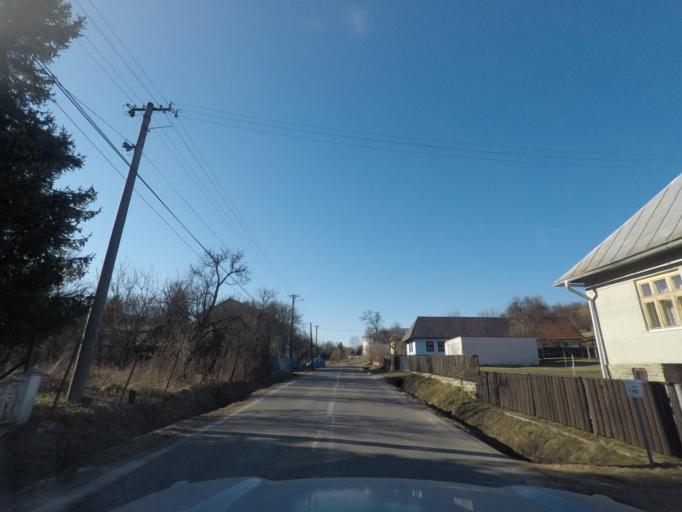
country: SK
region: Presovsky
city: Medzilaborce
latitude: 49.1955
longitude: 22.0015
